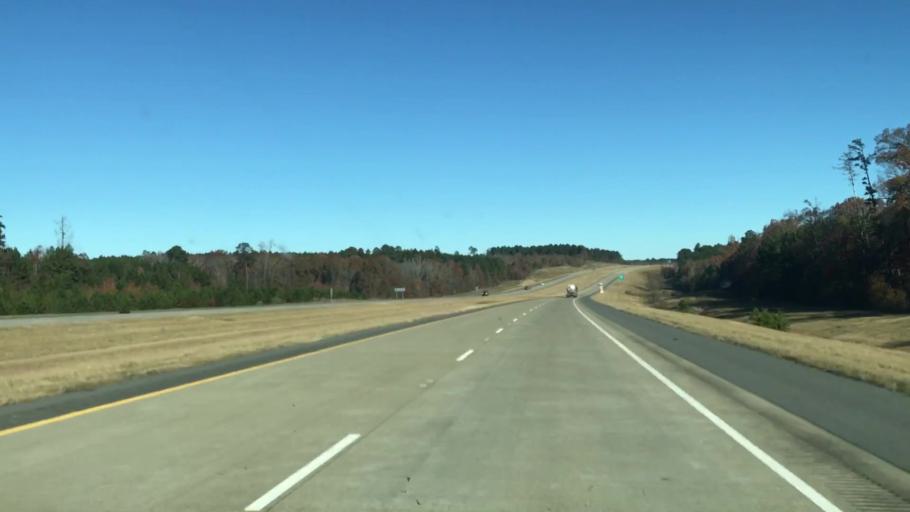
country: US
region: Louisiana
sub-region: Caddo Parish
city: Vivian
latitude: 32.9802
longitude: -93.9100
